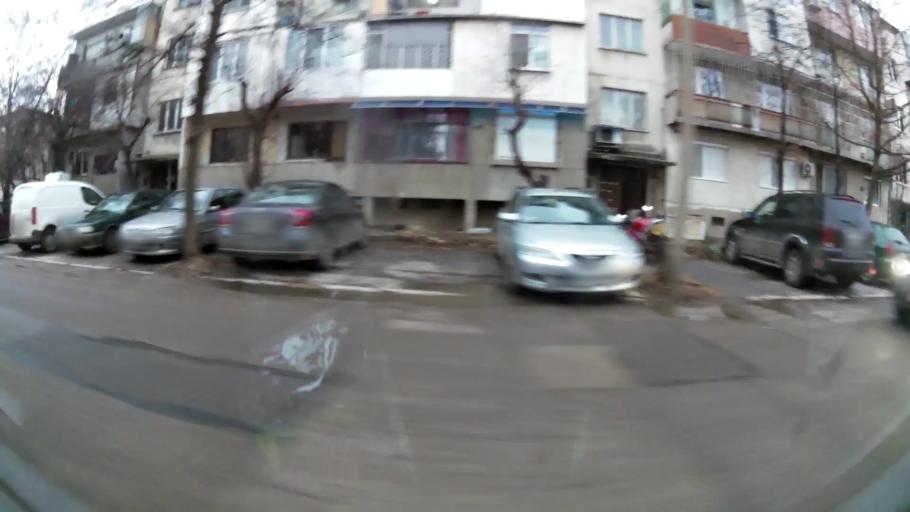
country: BG
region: Sofia-Capital
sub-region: Stolichna Obshtina
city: Sofia
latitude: 42.7340
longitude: 23.3002
